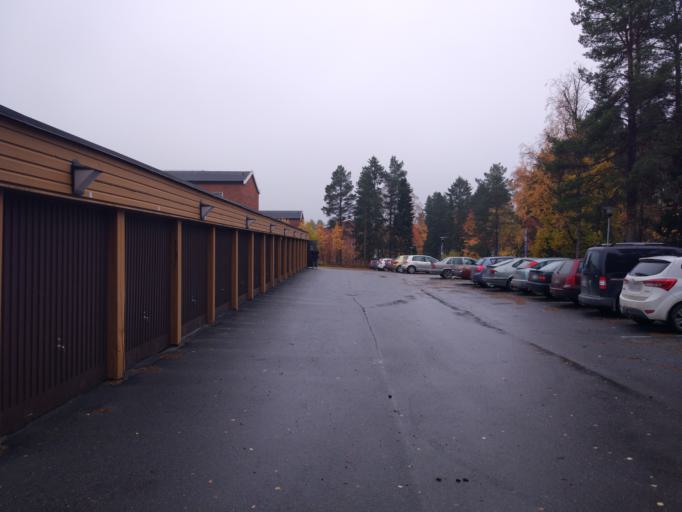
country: SE
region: Vaesterbotten
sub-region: Umea Kommun
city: Holmsund
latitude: 63.7067
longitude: 20.3725
